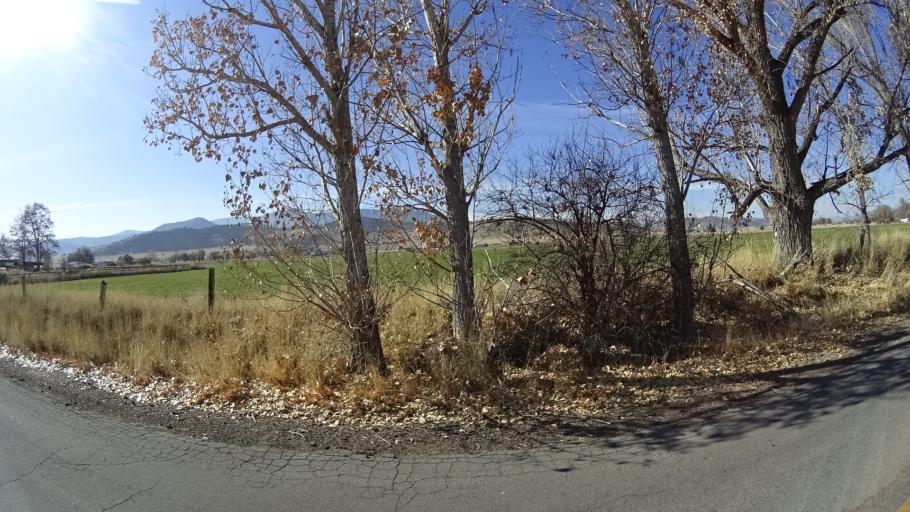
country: US
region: California
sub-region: Siskiyou County
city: Montague
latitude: 41.6366
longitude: -122.5217
